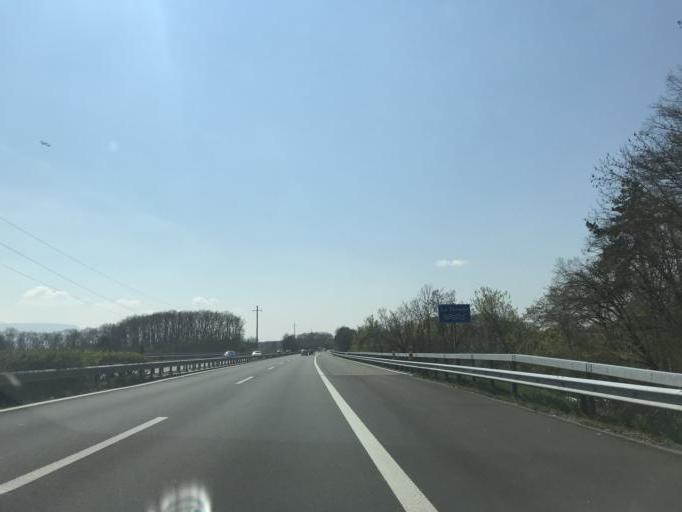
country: CH
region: Geneva
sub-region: Geneva
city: Versoix
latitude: 46.2825
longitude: 6.1441
